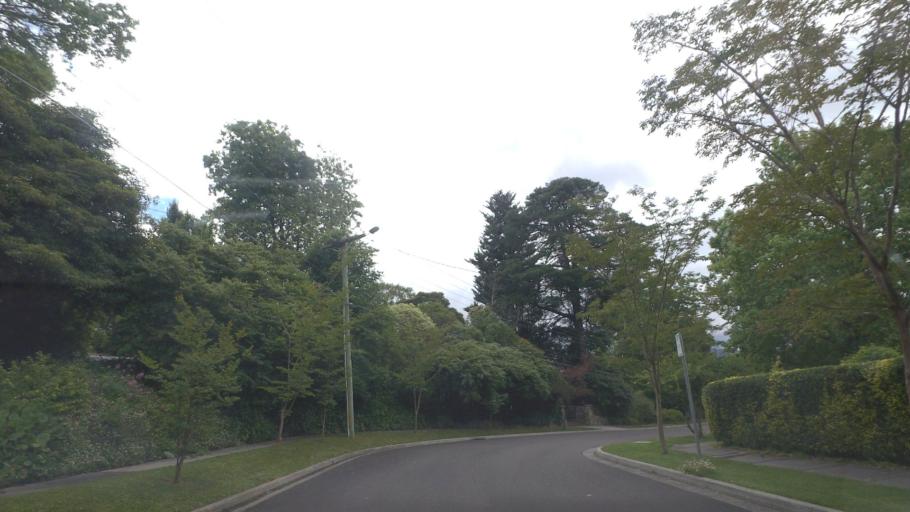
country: AU
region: Victoria
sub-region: Maroondah
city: Croydon South
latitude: -37.7959
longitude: 145.2750
